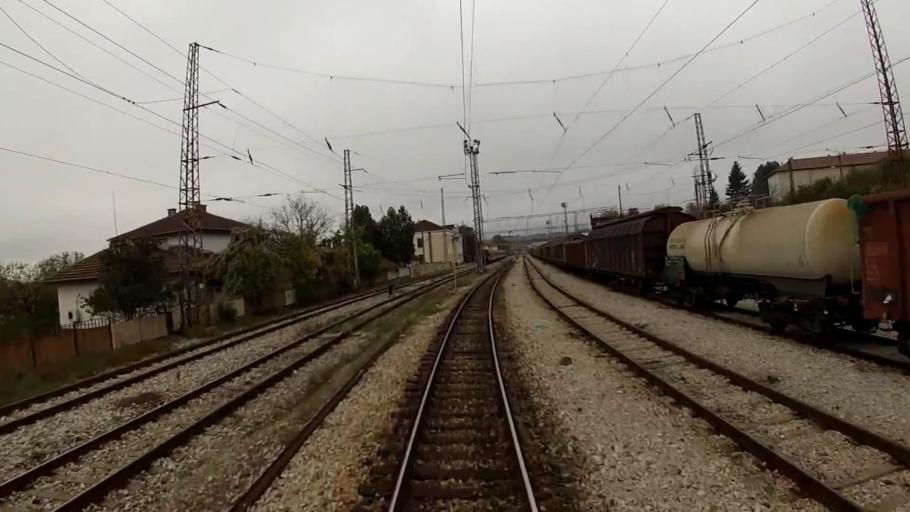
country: BG
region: Sofiya
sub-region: Obshtina Dragoman
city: Dragoman
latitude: 42.9272
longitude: 22.9329
